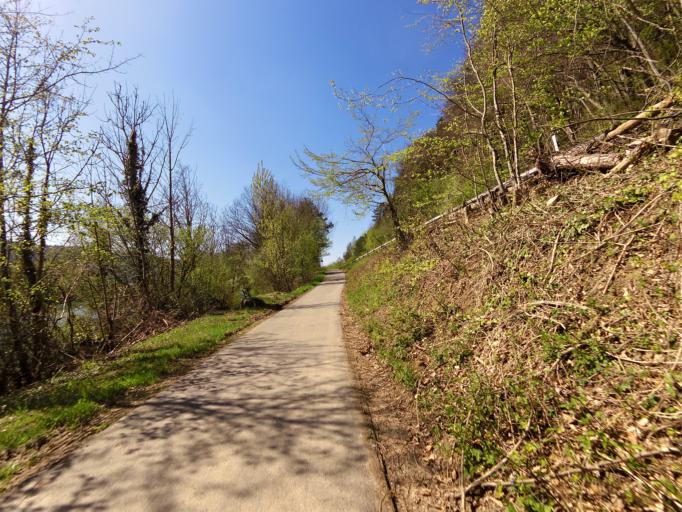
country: CH
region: Aargau
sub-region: Bezirk Zurzach
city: Bad Zurzach
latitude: 47.5710
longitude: 8.3554
